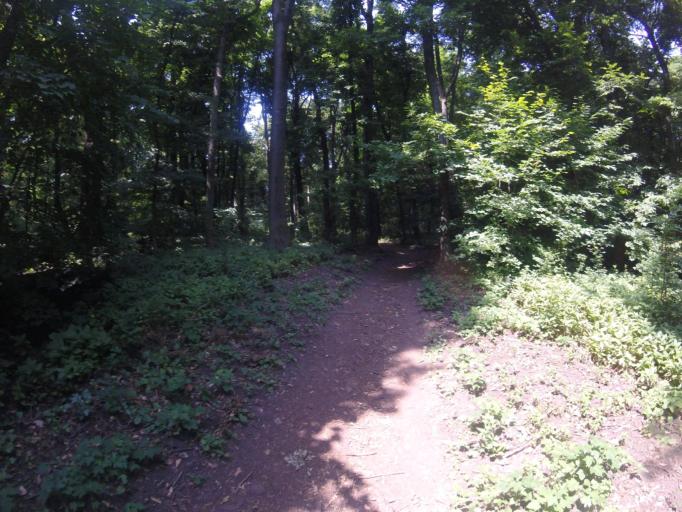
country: HU
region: Veszprem
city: Badacsonytomaj
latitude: 46.7986
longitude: 17.4969
